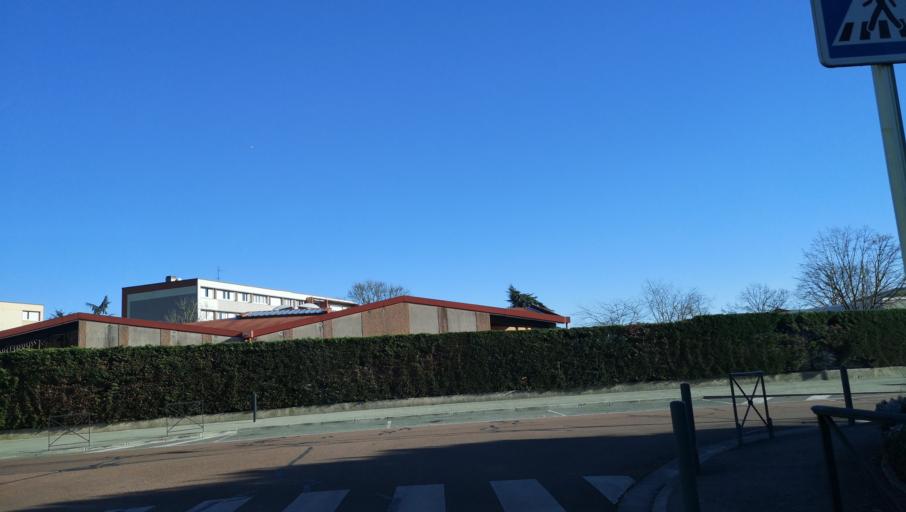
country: FR
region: Midi-Pyrenees
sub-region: Departement de la Haute-Garonne
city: Beauzelle
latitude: 43.6620
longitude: 1.3769
